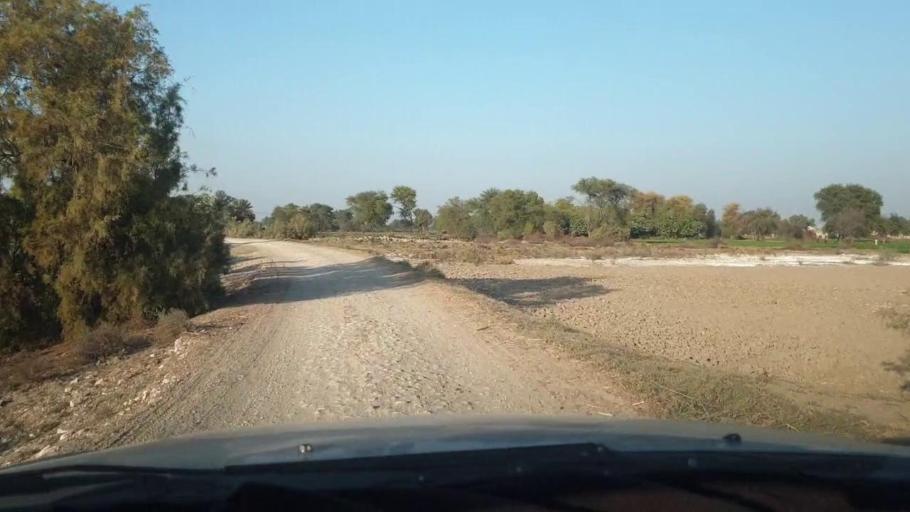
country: PK
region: Sindh
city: Mirpur Mathelo
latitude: 28.0016
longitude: 69.5037
